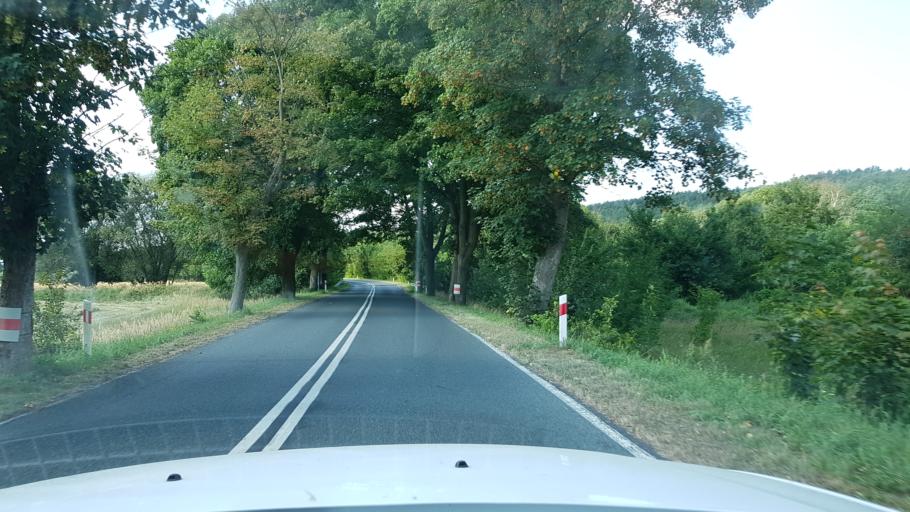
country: PL
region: West Pomeranian Voivodeship
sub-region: Powiat gryfinski
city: Cedynia
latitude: 52.8336
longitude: 14.2029
